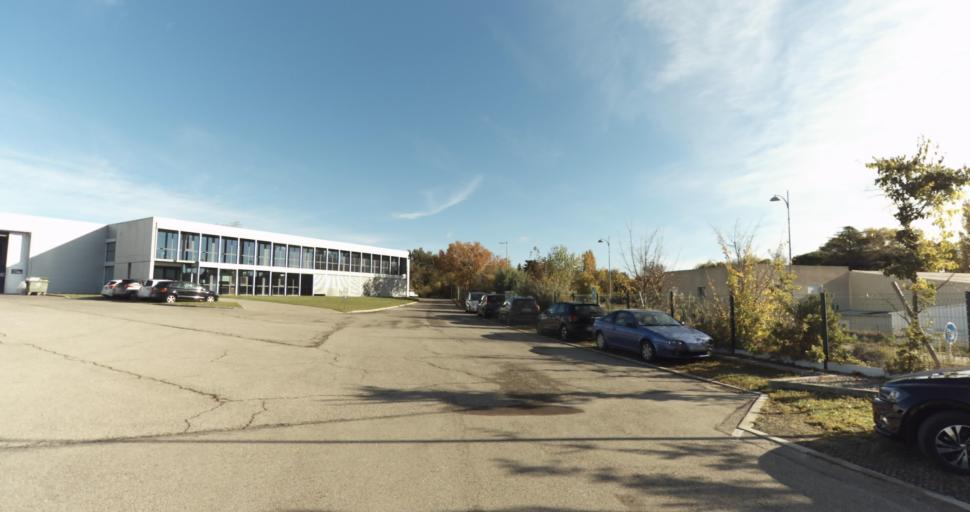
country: FR
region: Provence-Alpes-Cote d'Azur
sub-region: Departement des Bouches-du-Rhone
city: Venelles
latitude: 43.5830
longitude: 5.4673
